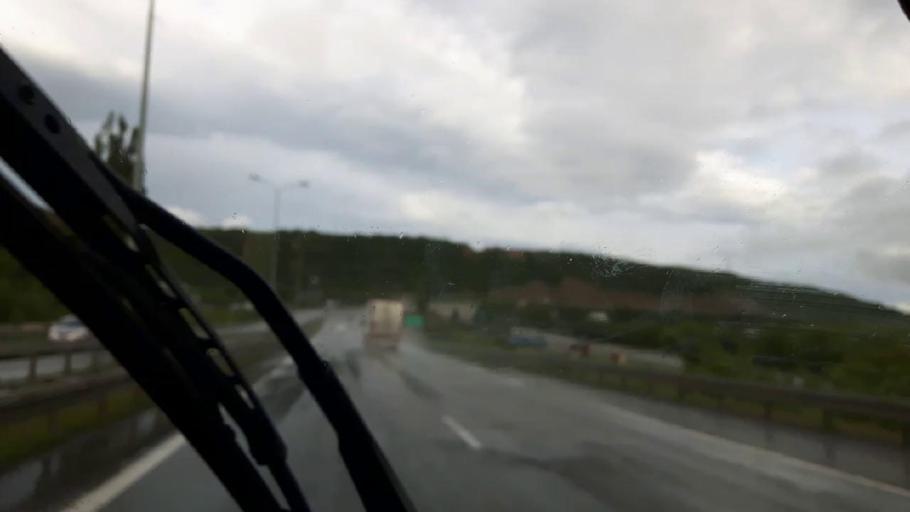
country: GE
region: Shida Kartli
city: Kaspi
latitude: 41.9931
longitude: 44.4165
